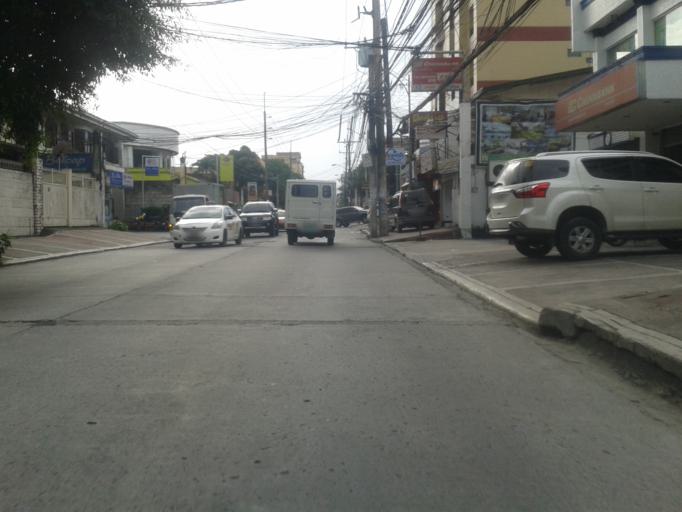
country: PH
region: Metro Manila
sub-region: Marikina
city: Calumpang
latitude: 14.6351
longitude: 121.0700
